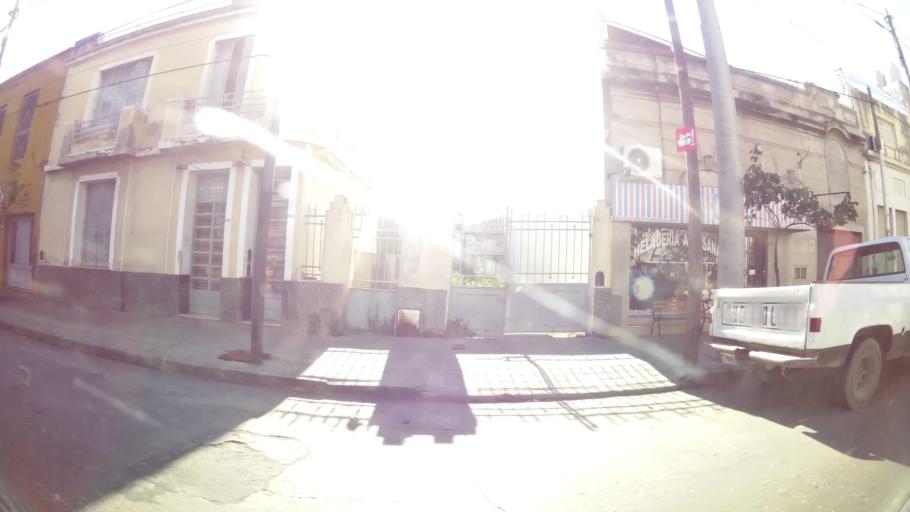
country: AR
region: Cordoba
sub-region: Departamento de Capital
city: Cordoba
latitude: -31.3931
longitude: -64.1760
